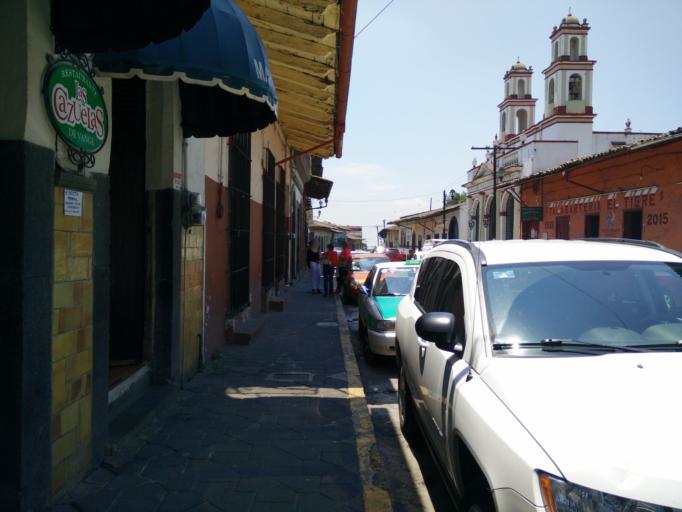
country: MX
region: Veracruz
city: Coatepec
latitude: 19.4536
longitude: -96.9562
